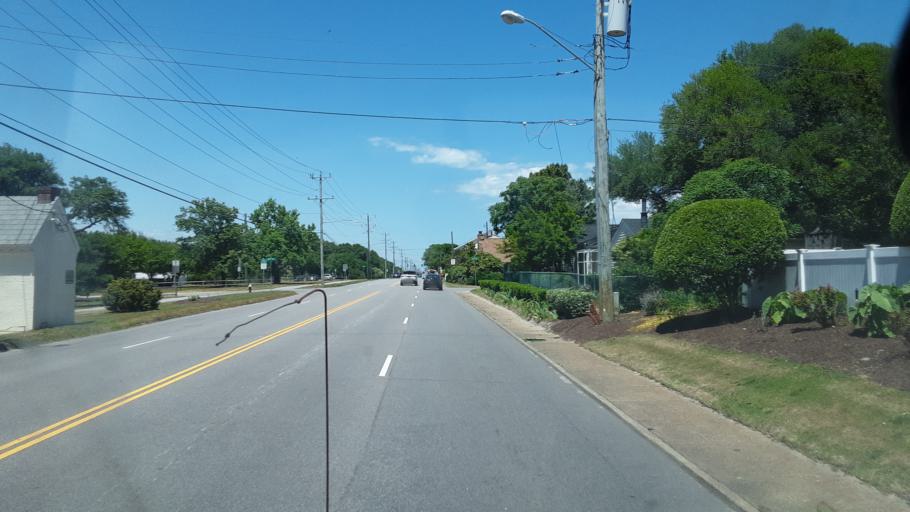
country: US
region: Virginia
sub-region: City of Virginia Beach
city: Virginia Beach
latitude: 36.8760
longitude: -75.9839
